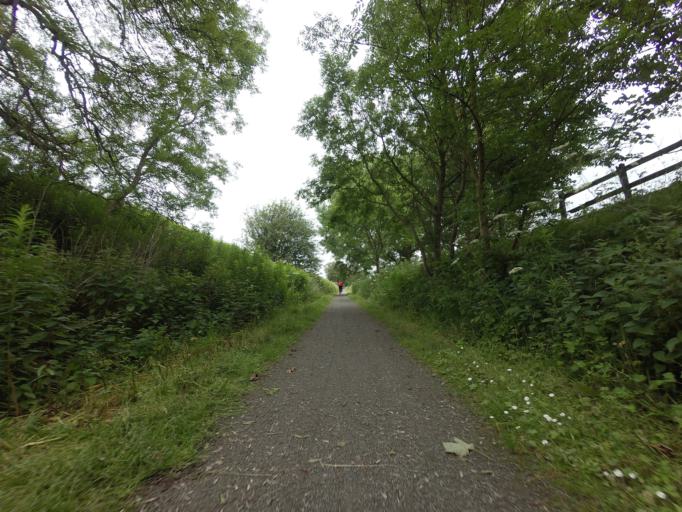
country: GB
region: Scotland
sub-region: Aberdeenshire
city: Mintlaw
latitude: 57.5135
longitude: -2.1386
